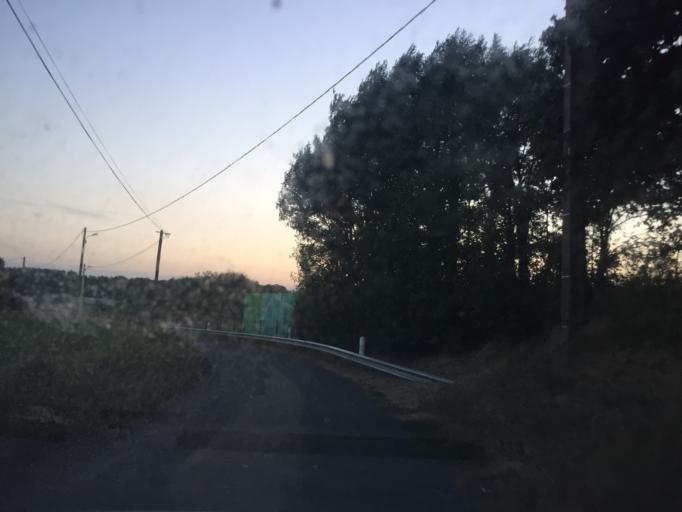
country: FR
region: Rhone-Alpes
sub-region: Departement de l'Ain
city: Mionnay
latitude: 45.8690
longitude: 4.9084
